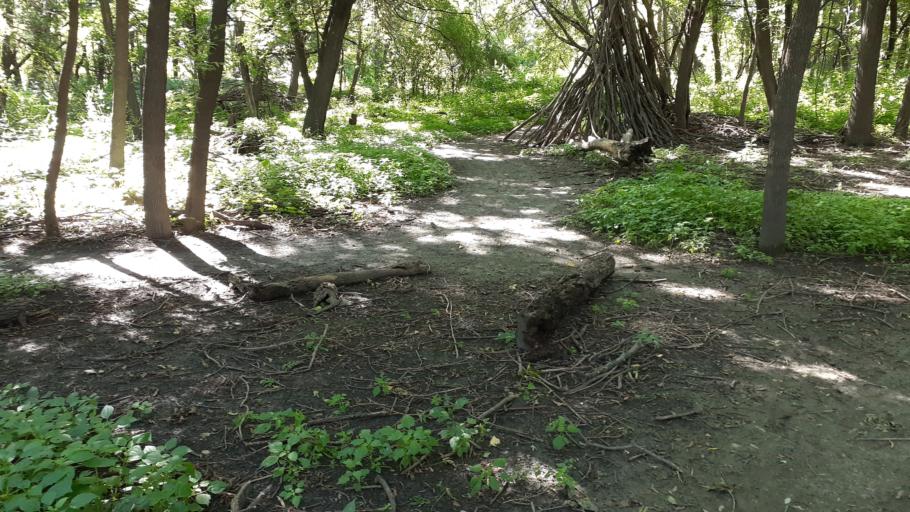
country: US
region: Minnesota
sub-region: Clay County
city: Oakport
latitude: 46.9142
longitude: -96.7608
